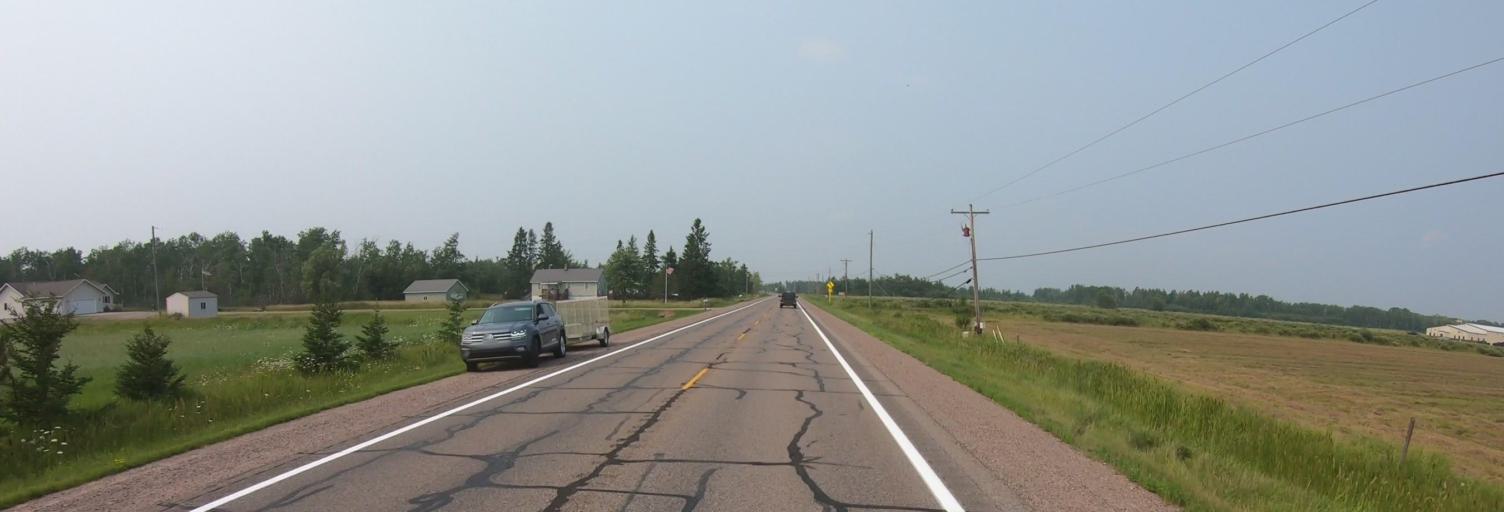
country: US
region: Michigan
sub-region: Chippewa County
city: Sault Ste. Marie
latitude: 46.4439
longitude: -84.3536
